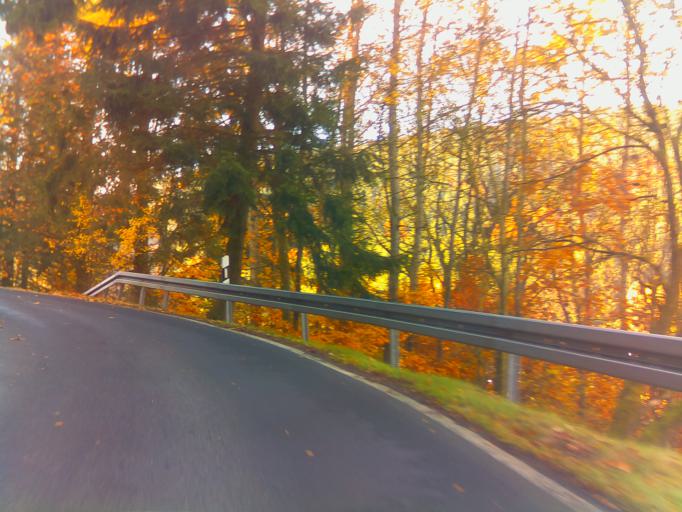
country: DE
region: Thuringia
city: Steinach
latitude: 50.4226
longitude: 11.1449
